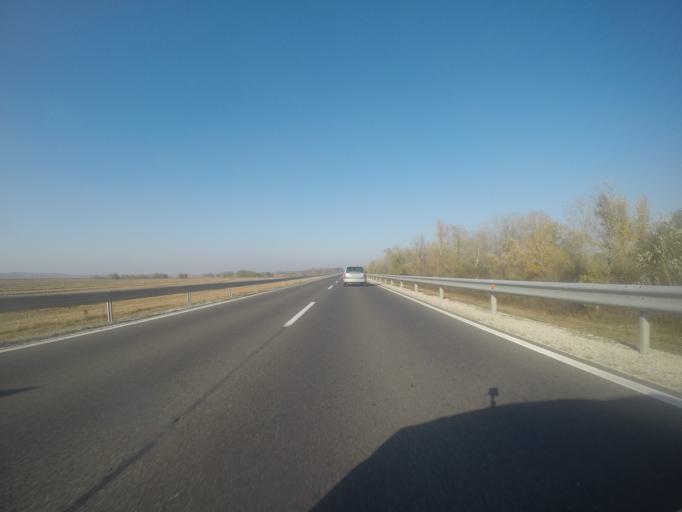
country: HU
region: Fejer
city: Adony
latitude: 47.1587
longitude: 18.8620
